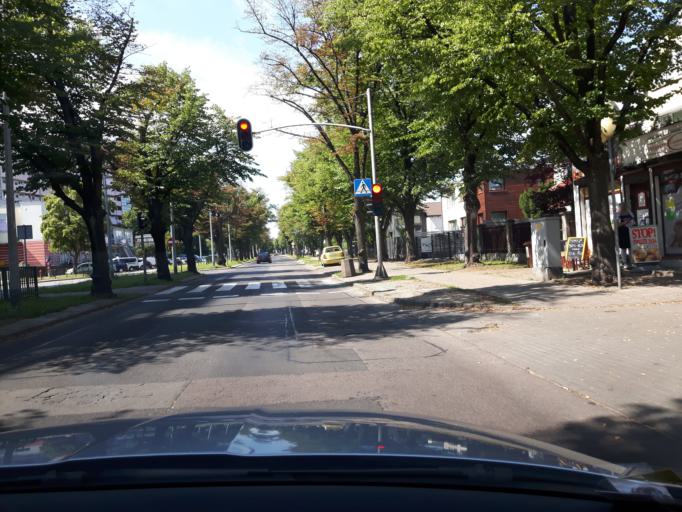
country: PL
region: Pomeranian Voivodeship
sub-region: Sopot
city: Sopot
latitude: 54.4173
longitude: 18.5919
